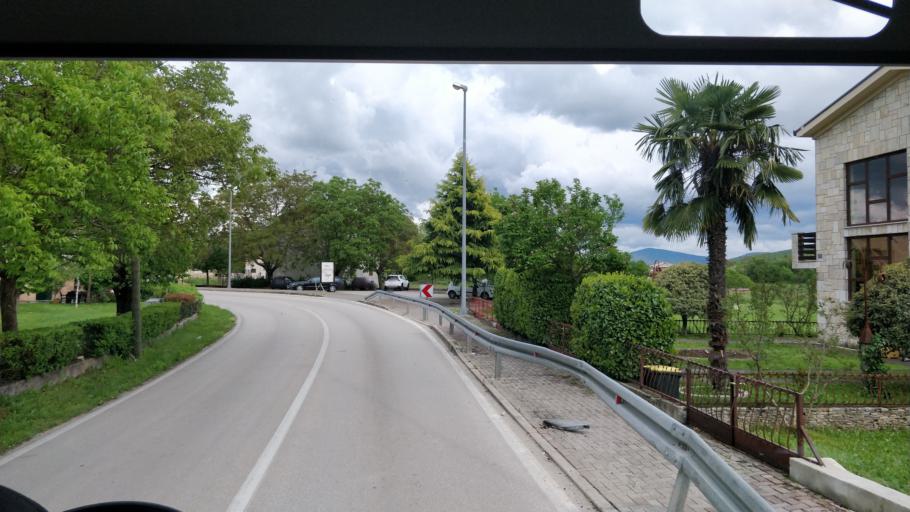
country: BA
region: Federation of Bosnia and Herzegovina
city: Ljubuski
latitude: 43.1810
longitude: 17.5195
